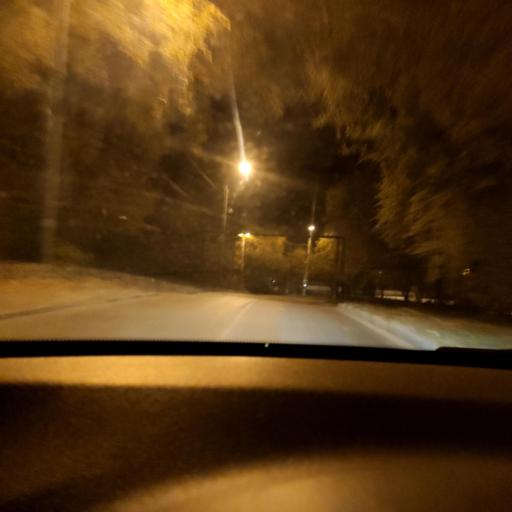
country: RU
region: Samara
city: Samara
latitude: 53.2434
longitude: 50.1738
